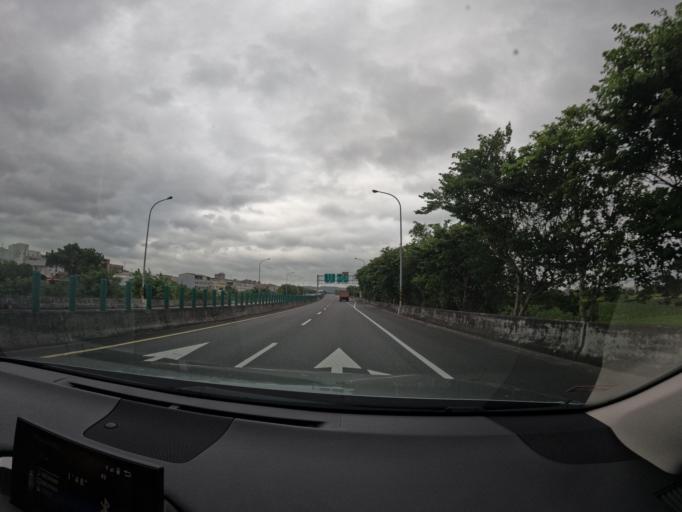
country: TW
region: Taiwan
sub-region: Miaoli
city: Miaoli
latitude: 24.4896
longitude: 120.8042
